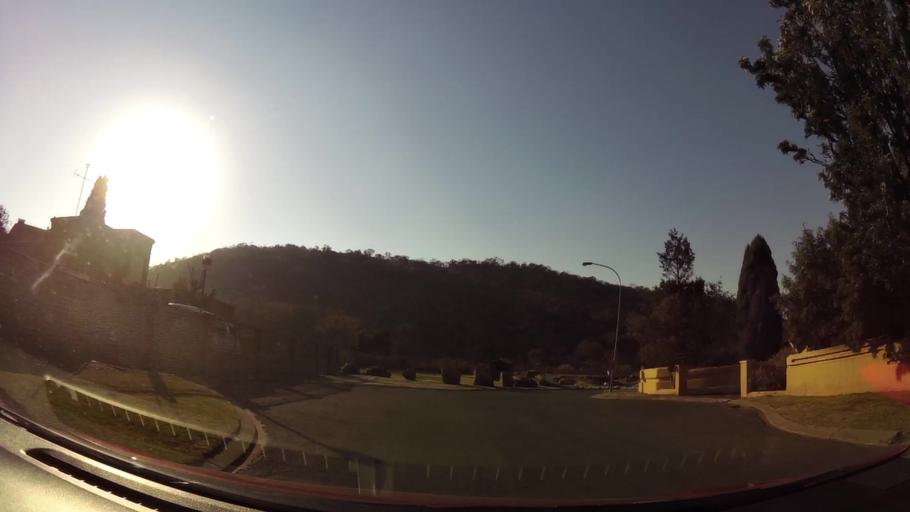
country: ZA
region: Gauteng
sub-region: City of Johannesburg Metropolitan Municipality
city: Soweto
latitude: -26.2893
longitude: 27.9605
